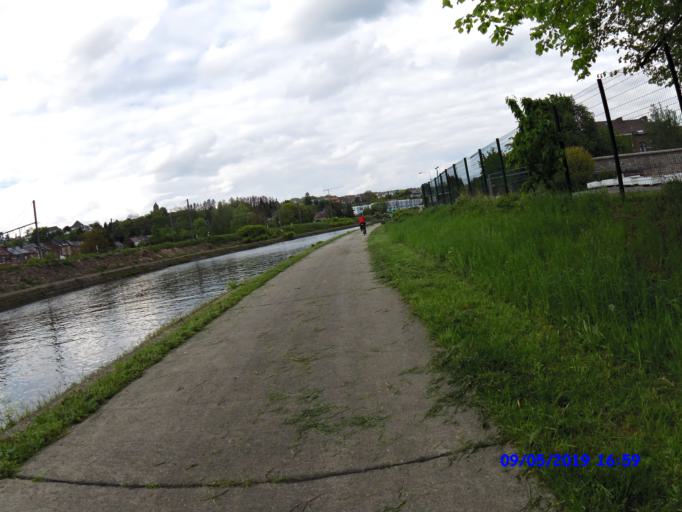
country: BE
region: Wallonia
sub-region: Province de Namur
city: Namur
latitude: 50.4666
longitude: 4.8357
